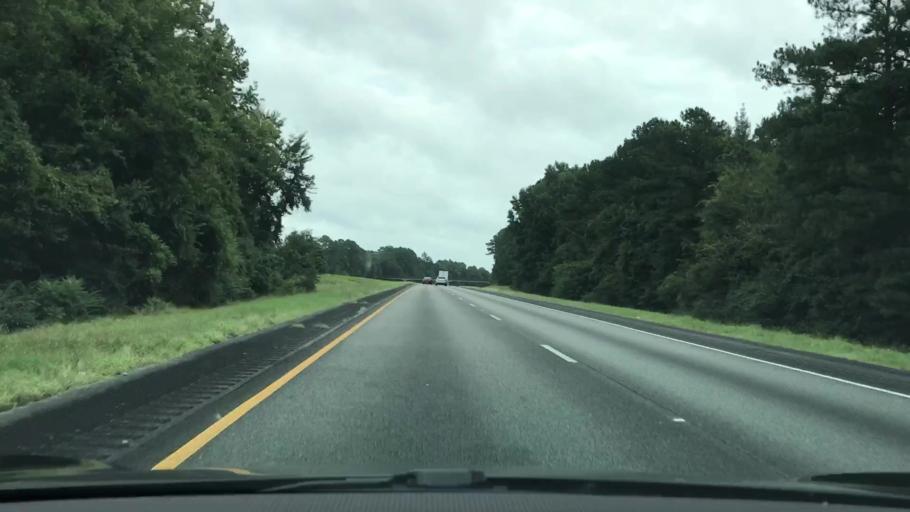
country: US
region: Alabama
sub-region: Elmore County
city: Tallassee
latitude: 32.4354
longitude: -85.8775
